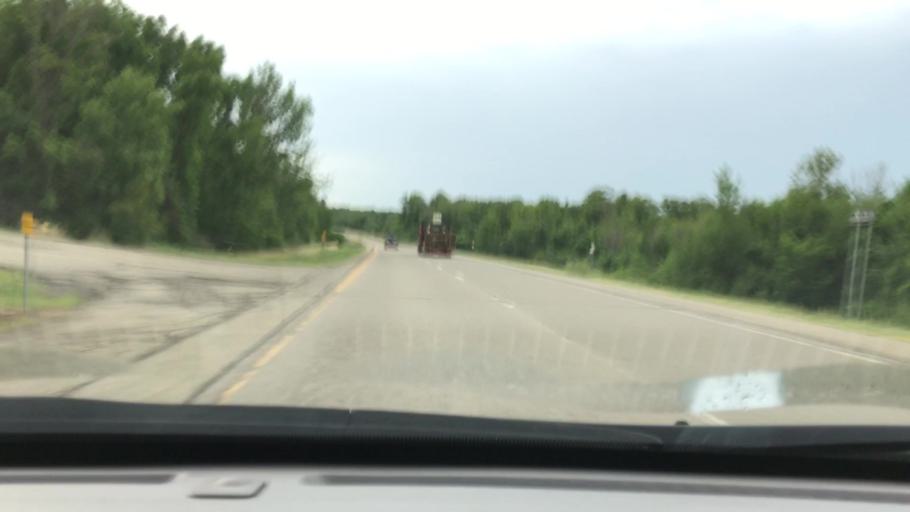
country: US
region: New York
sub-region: Erie County
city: North Boston
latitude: 42.6386
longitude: -78.7629
